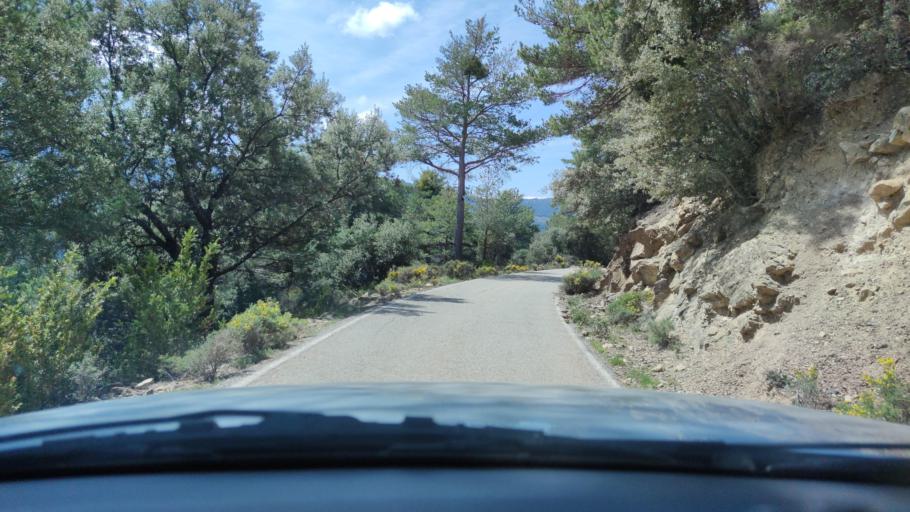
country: ES
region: Catalonia
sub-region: Provincia de Lleida
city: Sort
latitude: 42.3117
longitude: 1.1328
